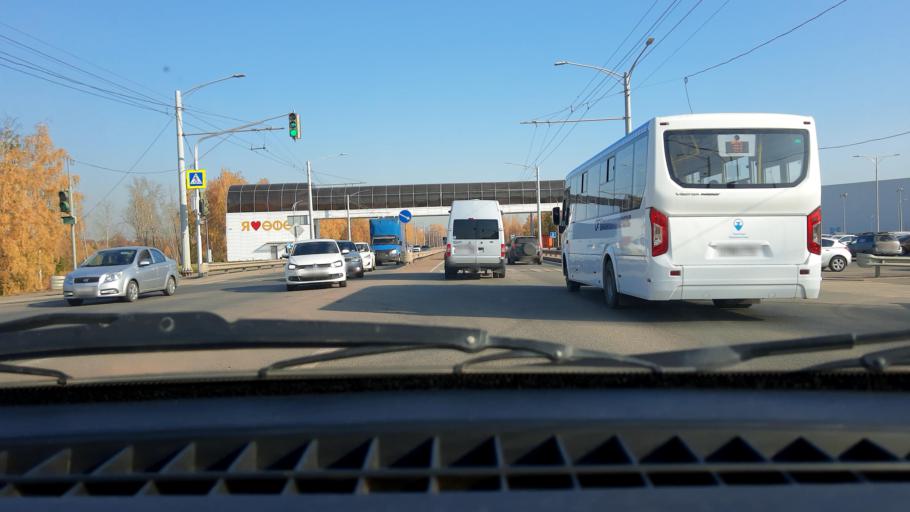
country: RU
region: Bashkortostan
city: Mikhaylovka
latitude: 54.7705
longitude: 55.9114
